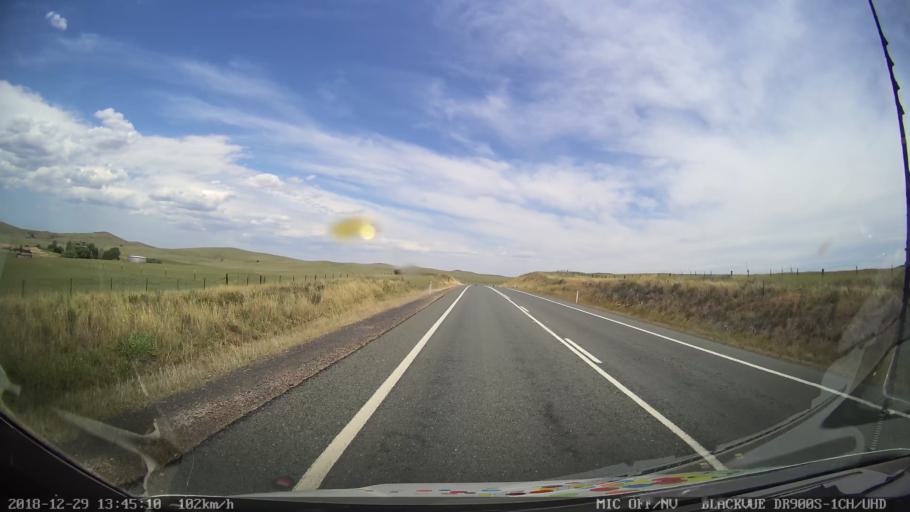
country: AU
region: New South Wales
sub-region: Cooma-Monaro
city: Cooma
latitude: -36.0923
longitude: 149.1452
